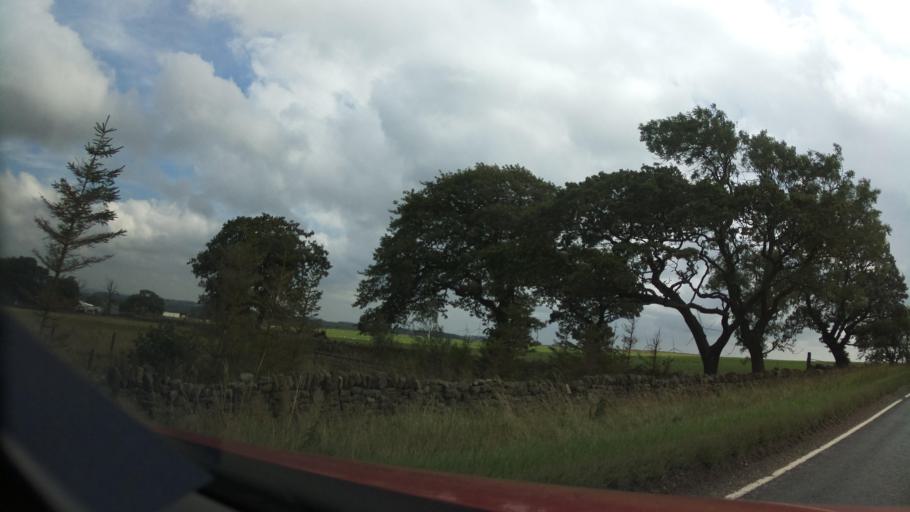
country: GB
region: England
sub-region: County Durham
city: Tow Law
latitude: 54.7767
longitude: -1.8532
